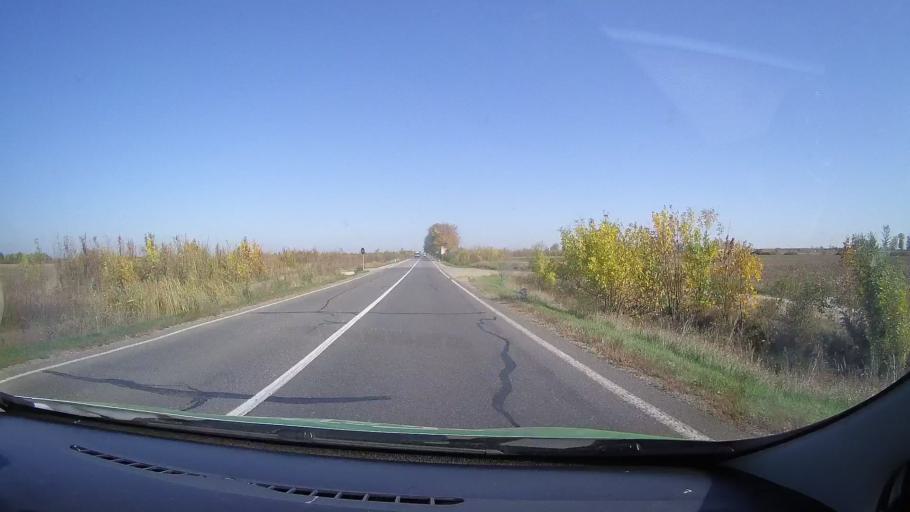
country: RO
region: Satu Mare
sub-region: Comuna Moftinu
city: Moftinu Mic
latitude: 47.6991
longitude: 22.6252
